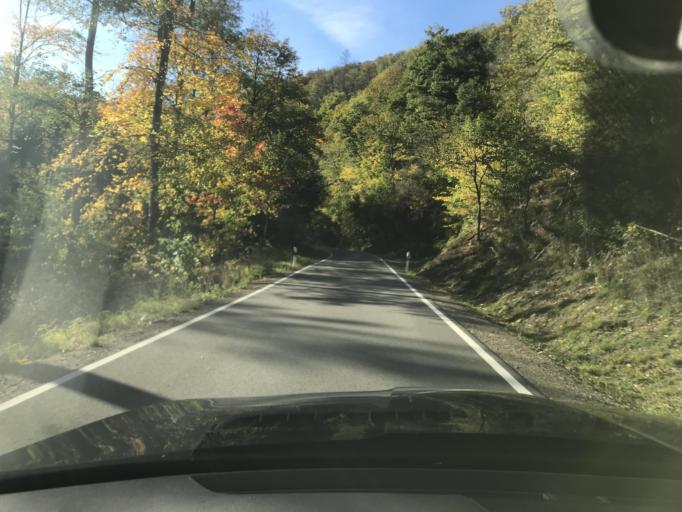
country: DE
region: Saxony-Anhalt
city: Friedrichsbrunn
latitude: 51.6978
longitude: 10.9640
